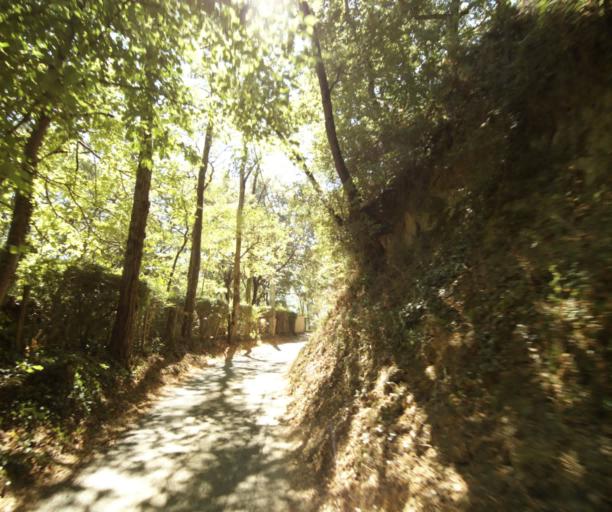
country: FR
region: Midi-Pyrenees
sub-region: Departement de la Haute-Garonne
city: Castanet-Tolosan
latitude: 43.5084
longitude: 1.4928
